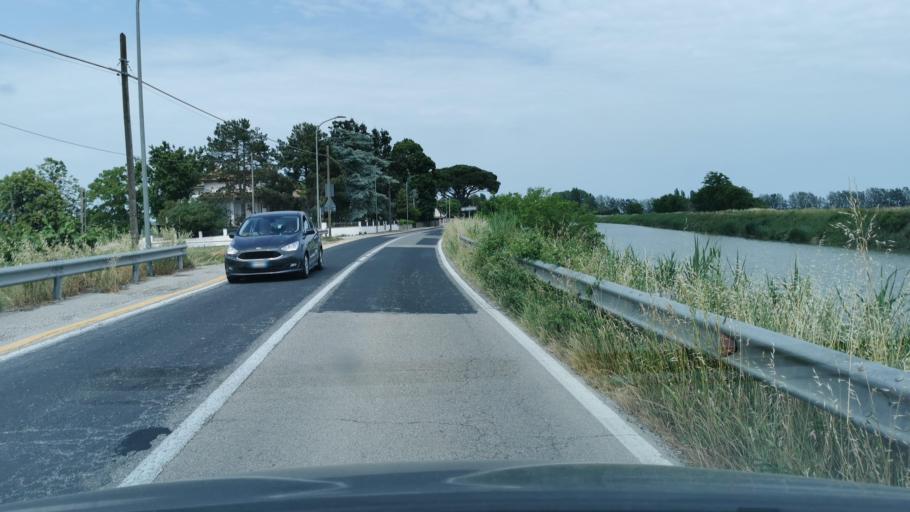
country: IT
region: Emilia-Romagna
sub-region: Provincia di Ravenna
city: Marina Romea
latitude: 44.5536
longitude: 12.2265
